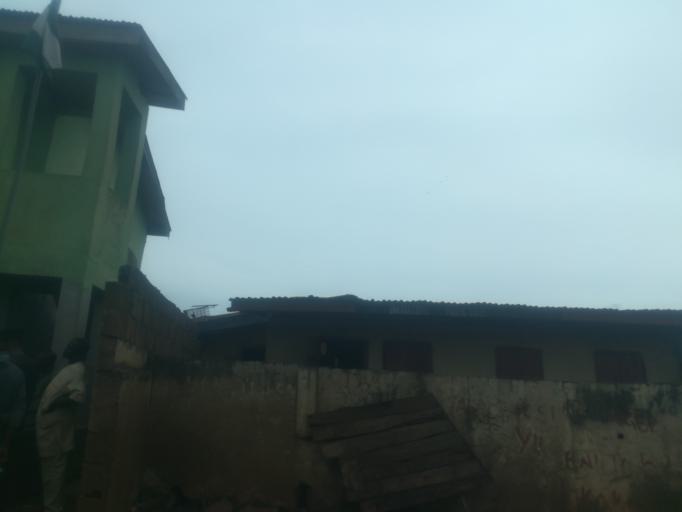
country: NG
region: Oyo
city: Ibadan
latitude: 7.3783
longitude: 3.9468
